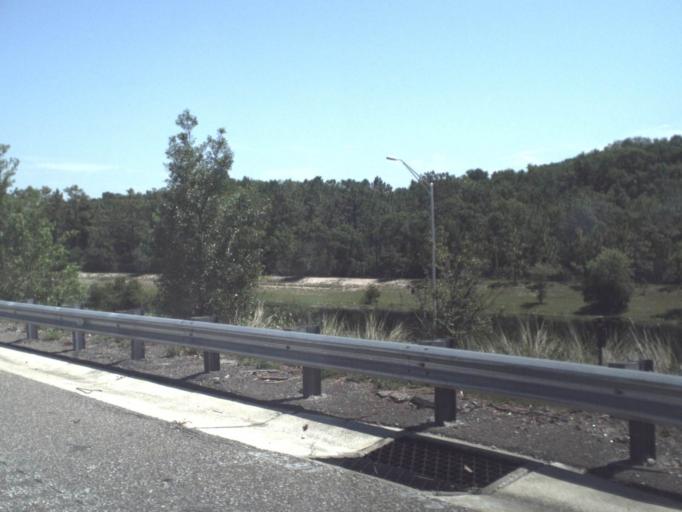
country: US
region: Florida
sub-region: Duval County
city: Jacksonville Beach
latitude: 30.2699
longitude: -81.5206
